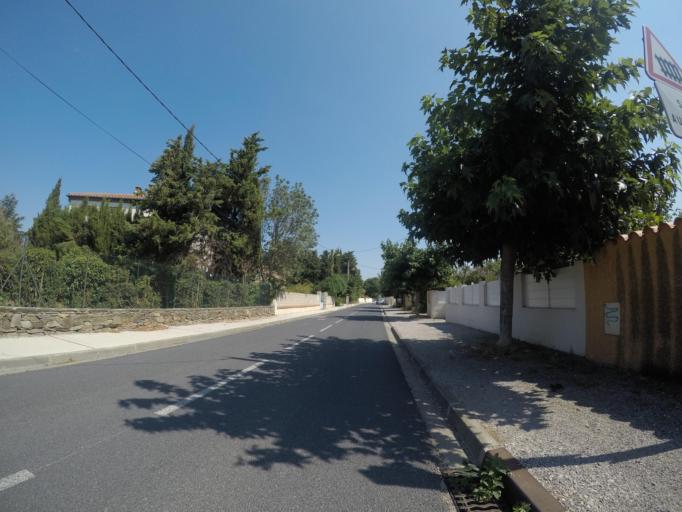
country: FR
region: Languedoc-Roussillon
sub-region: Departement des Pyrenees-Orientales
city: Millas
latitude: 42.6881
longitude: 2.6913
